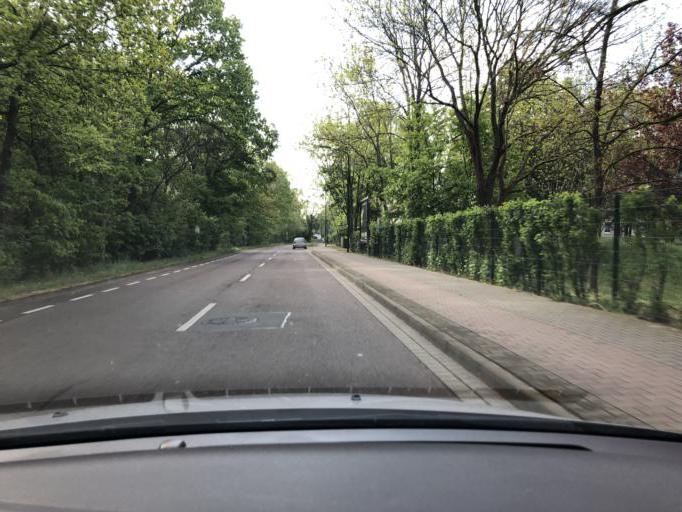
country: DE
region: Saxony
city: Markkleeberg
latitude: 51.2469
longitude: 12.3814
